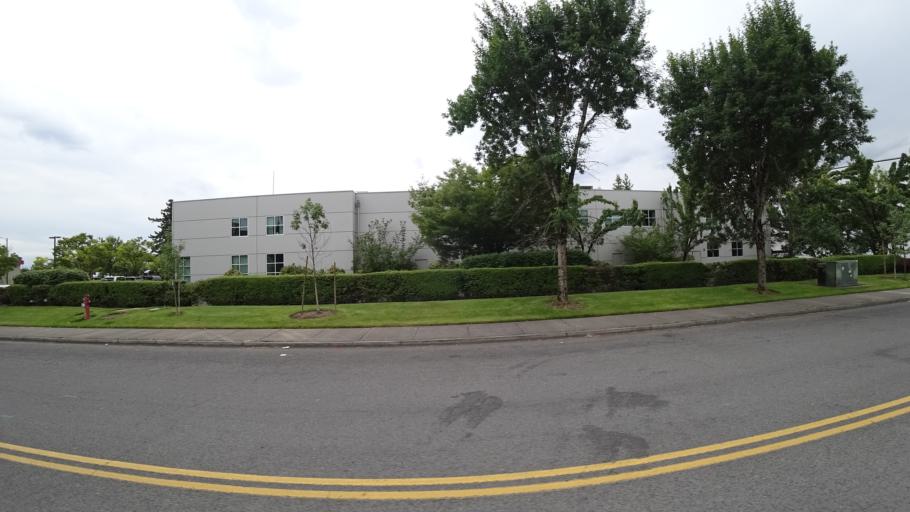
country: US
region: Oregon
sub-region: Multnomah County
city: Fairview
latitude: 45.5407
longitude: -122.4809
